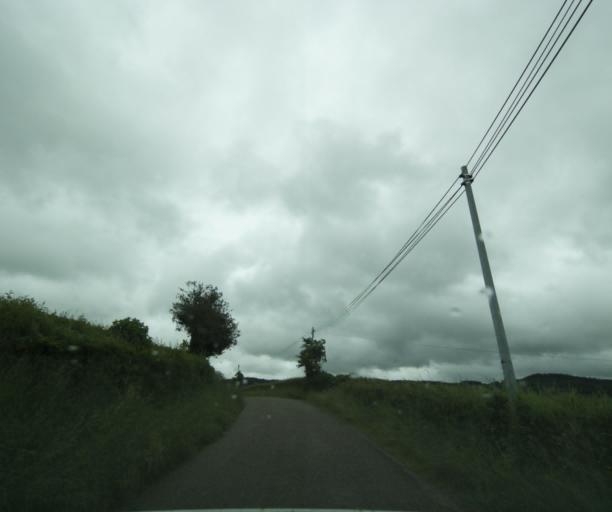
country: FR
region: Bourgogne
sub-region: Departement de Saone-et-Loire
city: Matour
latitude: 46.4568
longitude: 4.4543
